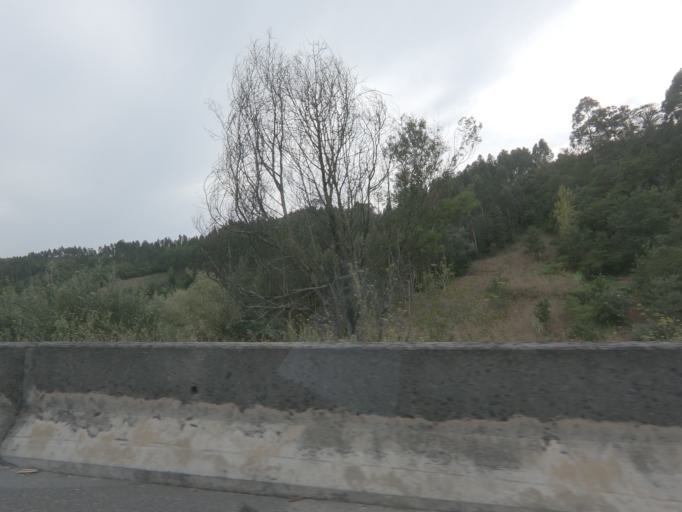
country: PT
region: Aveiro
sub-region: Mealhada
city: Pampilhosa do Botao
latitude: 40.3039
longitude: -8.3949
